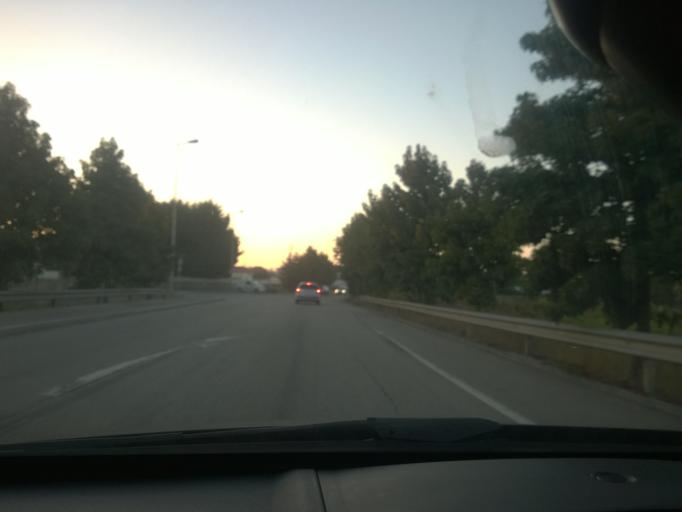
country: PT
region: Porto
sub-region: Matosinhos
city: Santa Cruz do Bispo
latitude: 41.2269
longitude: -8.6973
